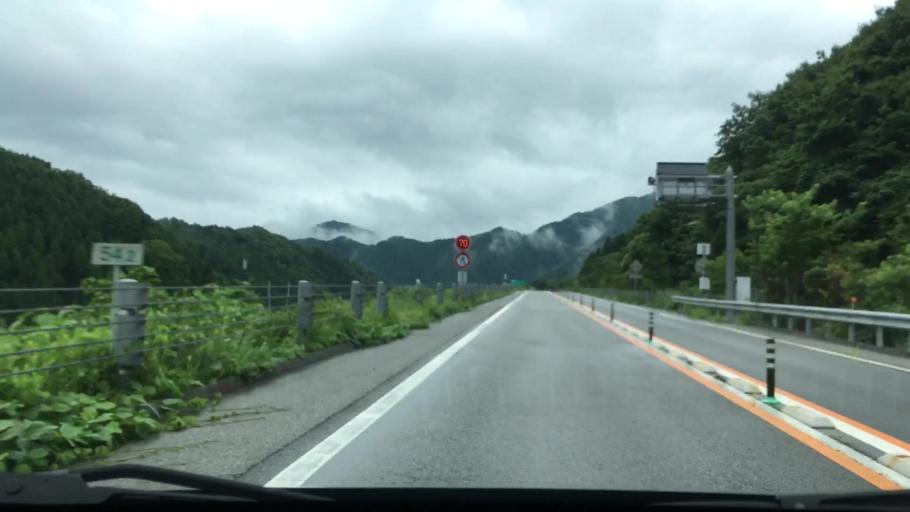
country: JP
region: Hyogo
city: Toyooka
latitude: 35.2488
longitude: 134.7911
